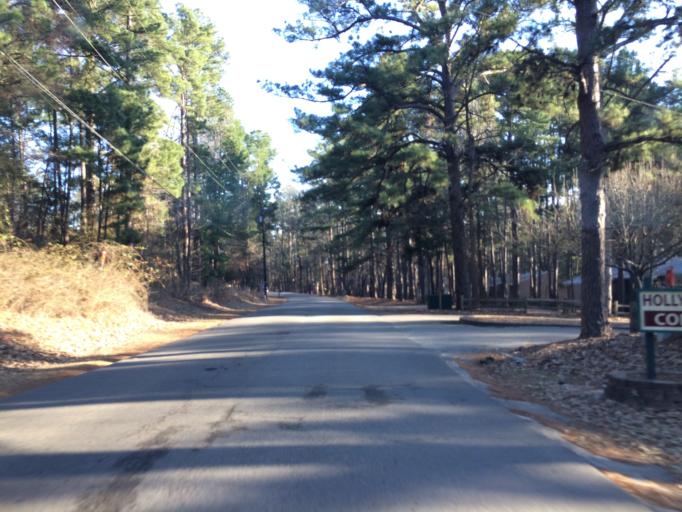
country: US
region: Texas
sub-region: Wood County
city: Hawkins
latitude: 32.7132
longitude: -95.1953
